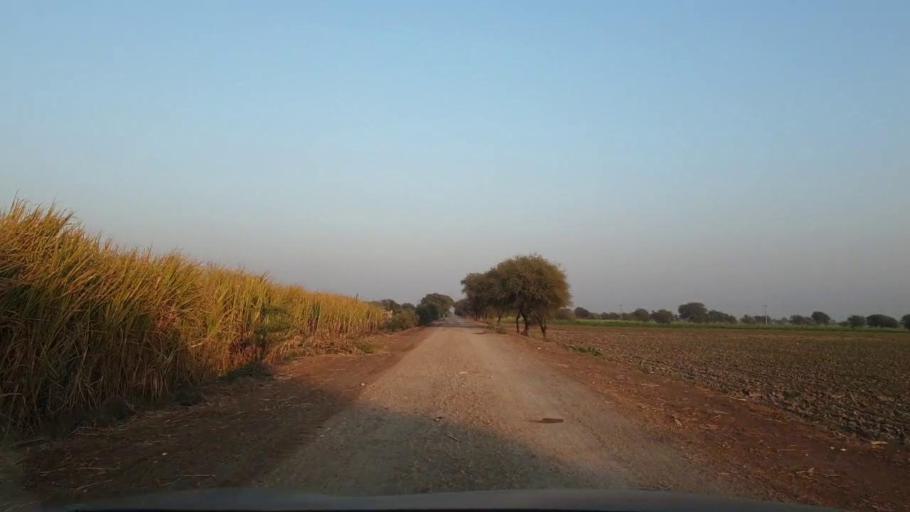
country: PK
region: Sindh
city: Mirpur Khas
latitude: 25.5758
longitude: 68.8531
